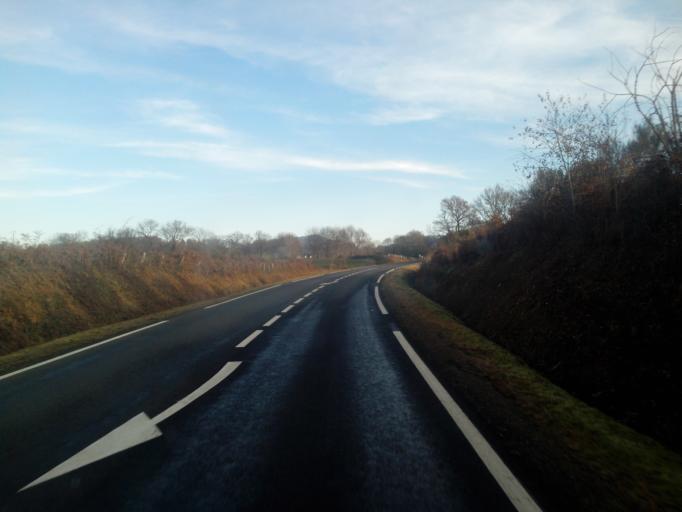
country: FR
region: Limousin
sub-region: Departement de la Correze
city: Bort-les-Orgues
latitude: 45.3570
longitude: 2.5105
